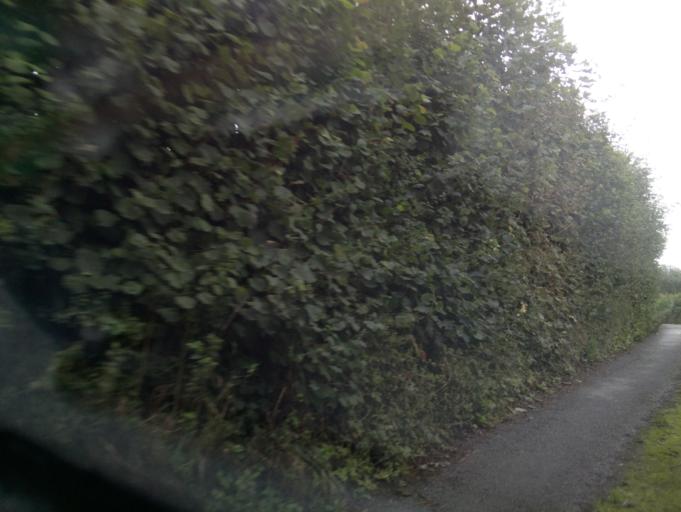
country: GB
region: England
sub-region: Devon
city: Dartmouth
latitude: 50.3334
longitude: -3.6015
